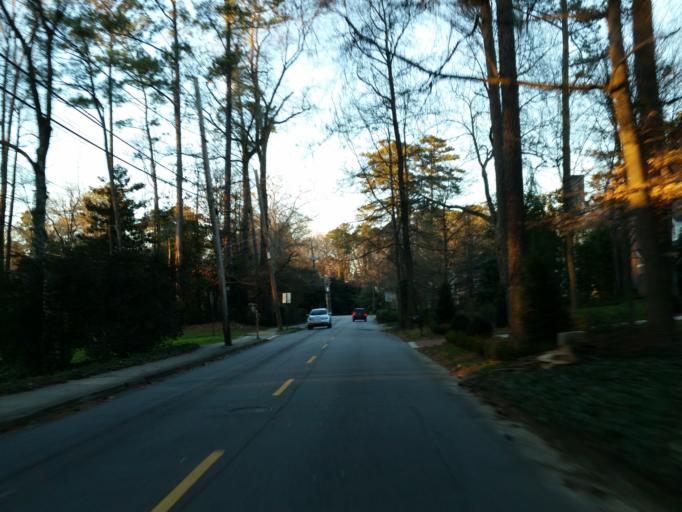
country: US
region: Georgia
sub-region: Cobb County
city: Vinings
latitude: 33.8269
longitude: -84.4293
